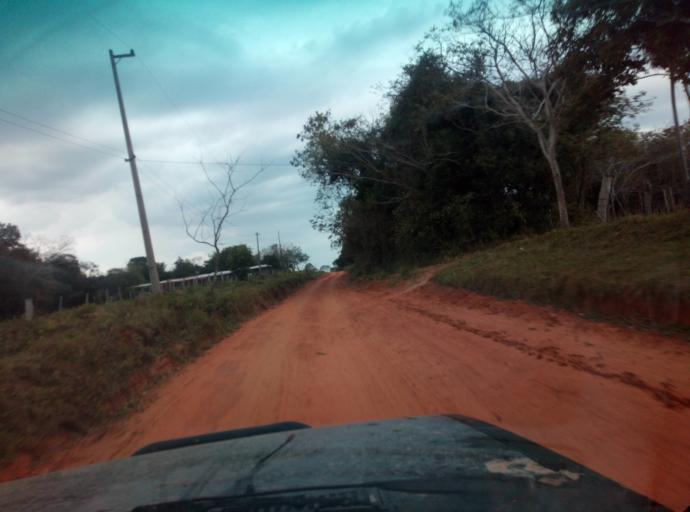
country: PY
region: Caaguazu
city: Doctor Cecilio Baez
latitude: -25.1392
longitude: -56.2236
